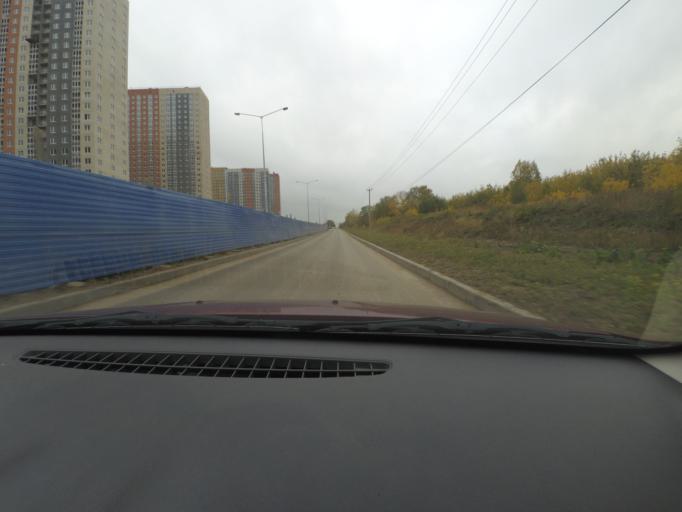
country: RU
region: Nizjnij Novgorod
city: Afonino
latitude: 56.2493
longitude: 44.0490
